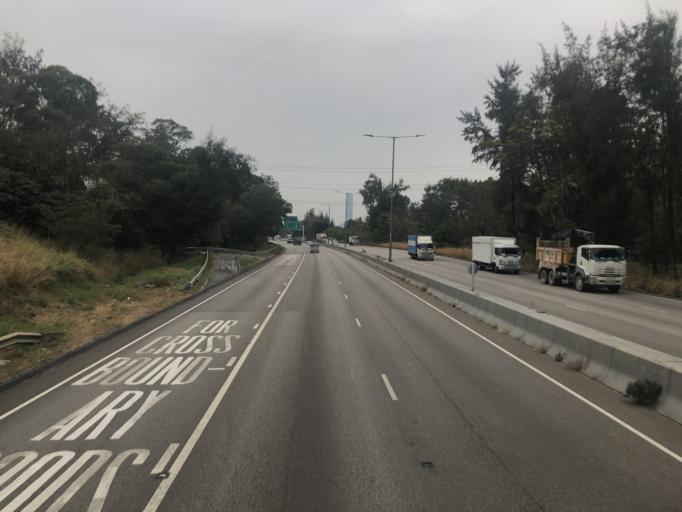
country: CN
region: Guangdong
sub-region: Shenzhen
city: Shenzhen
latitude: 22.5041
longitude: 114.0912
